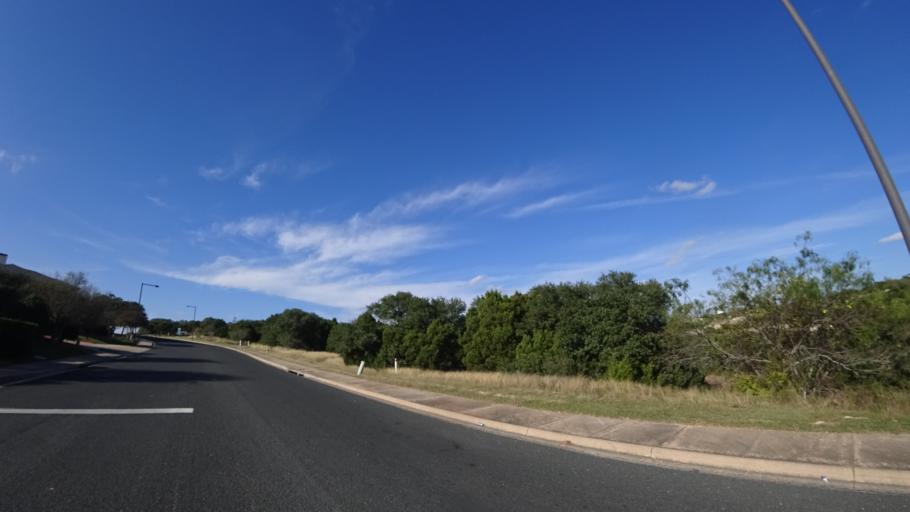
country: US
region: Texas
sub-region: Travis County
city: Barton Creek
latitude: 30.2510
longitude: -97.8687
